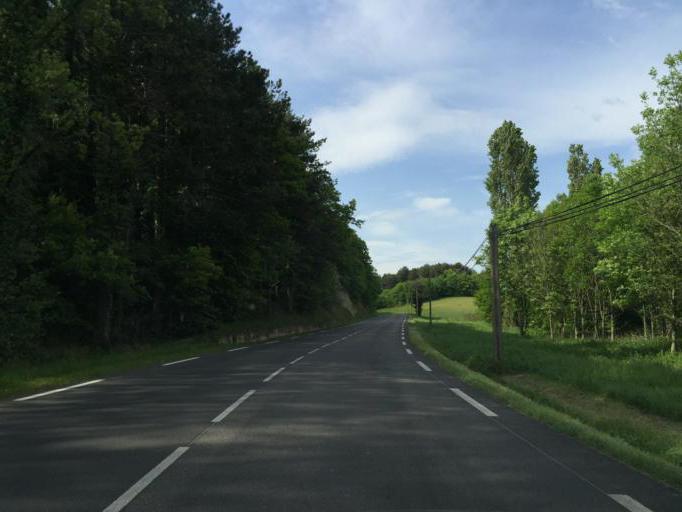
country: FR
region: Rhone-Alpes
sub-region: Departement de la Drome
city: Eurre
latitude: 44.7860
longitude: 5.0242
